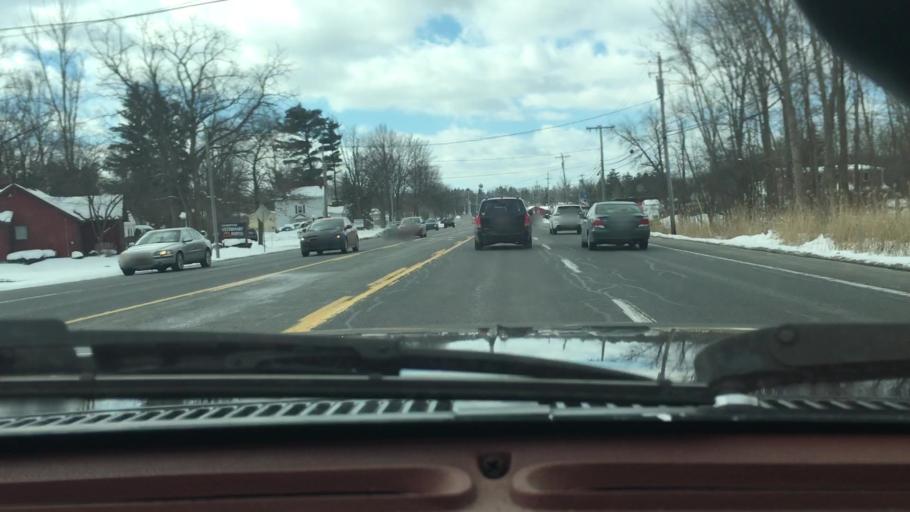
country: US
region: New York
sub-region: Onondaga County
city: Liverpool
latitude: 43.1541
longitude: -76.2278
